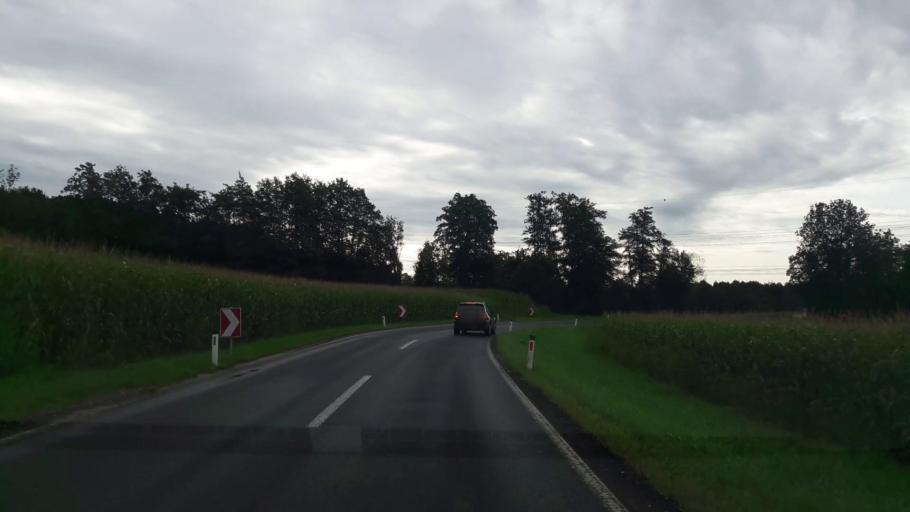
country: AT
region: Styria
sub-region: Politischer Bezirk Hartberg-Fuerstenfeld
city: Ebersdorf
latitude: 47.2076
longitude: 15.9445
